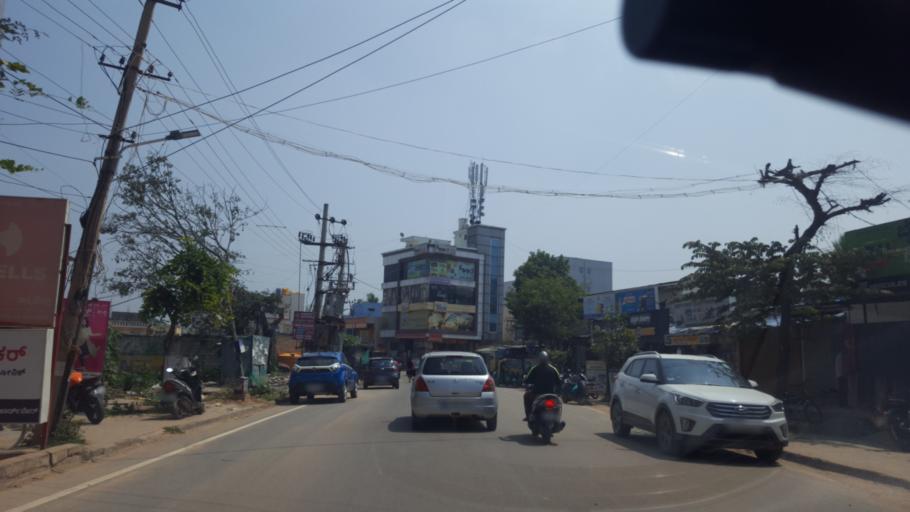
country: IN
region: Karnataka
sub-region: Bangalore Urban
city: Bangalore
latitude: 12.9368
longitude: 77.7032
